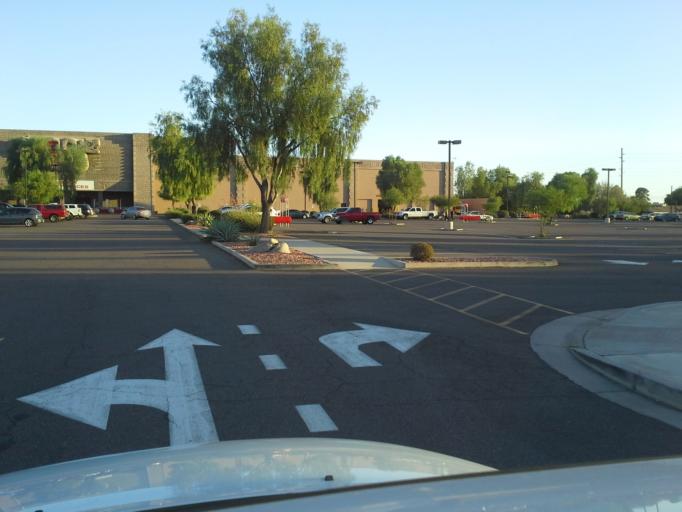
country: US
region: Arizona
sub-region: Maricopa County
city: Glendale
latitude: 33.6106
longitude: -112.1239
